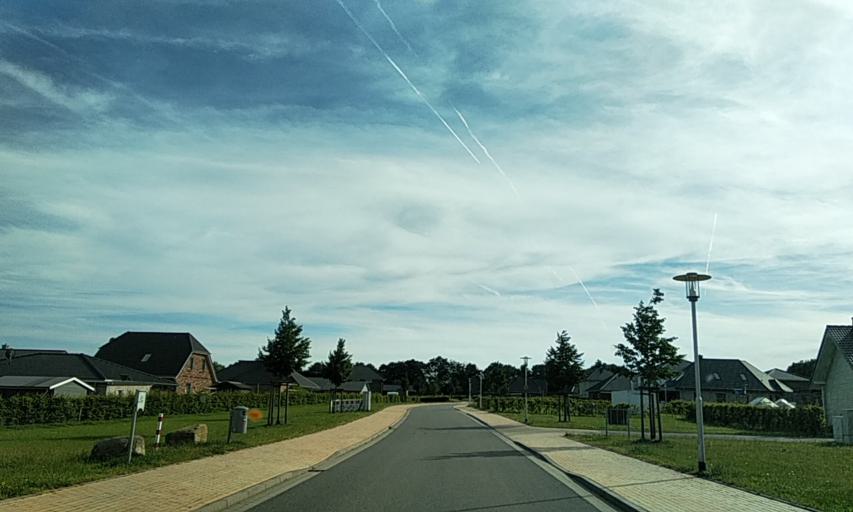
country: DE
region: Schleswig-Holstein
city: Schleswig
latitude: 54.5363
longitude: 9.5647
